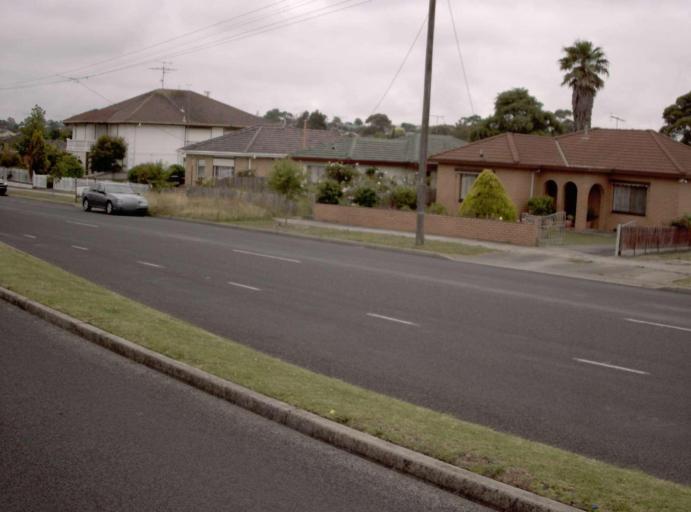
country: AU
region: Victoria
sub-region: Latrobe
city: Morwell
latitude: -38.2378
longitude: 146.4049
